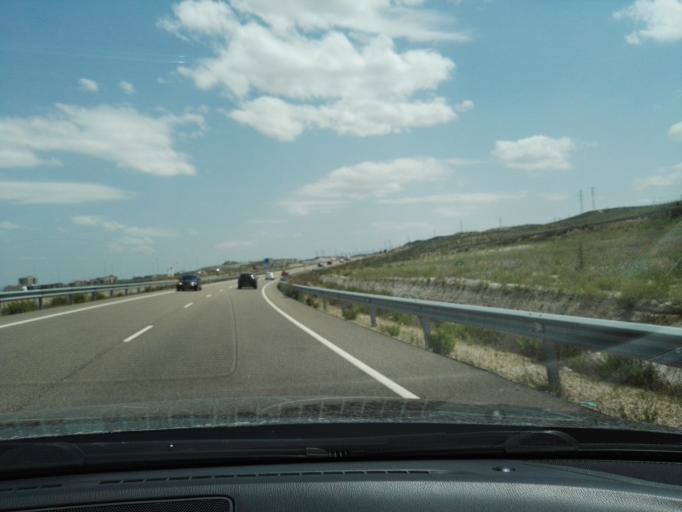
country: ES
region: Aragon
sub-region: Provincia de Zaragoza
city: Montecanal
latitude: 41.6211
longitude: -0.9742
